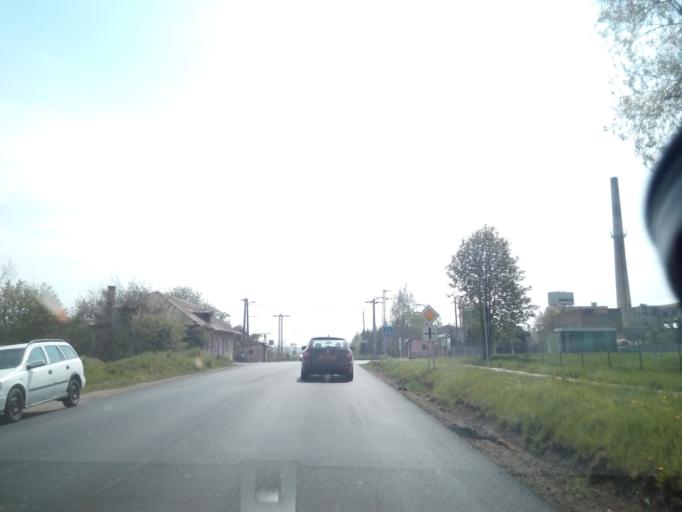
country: SK
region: Presovsky
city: Giraltovce
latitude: 49.0059
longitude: 21.5427
